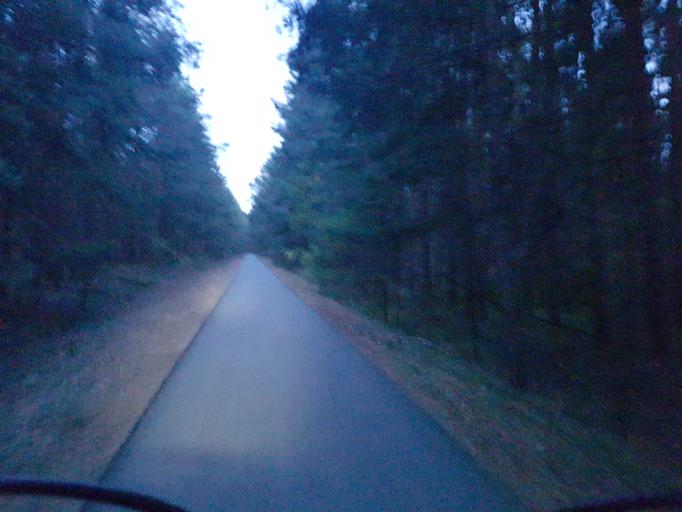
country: DE
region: Brandenburg
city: Trobitz
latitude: 51.5658
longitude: 13.4419
